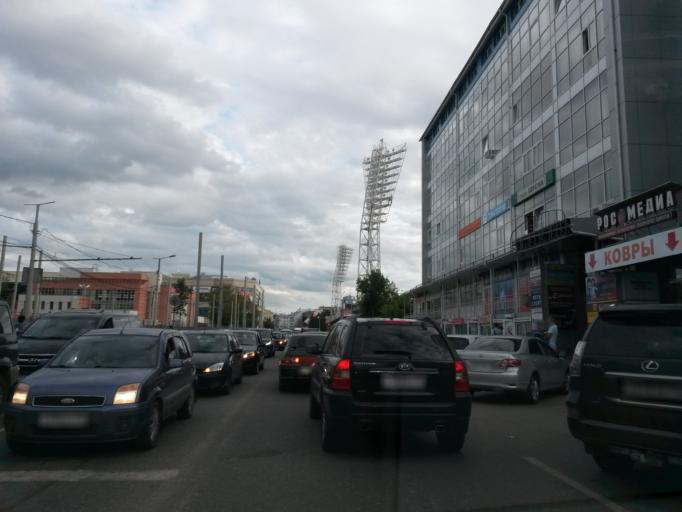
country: RU
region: Jaroslavl
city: Yaroslavl
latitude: 57.6305
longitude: 39.8696
